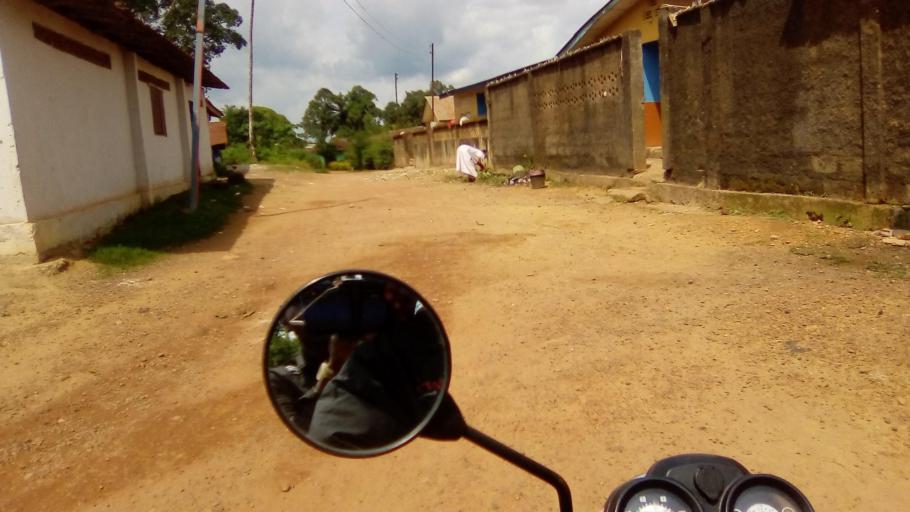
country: SL
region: Southern Province
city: Bo
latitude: 7.9518
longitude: -11.7299
